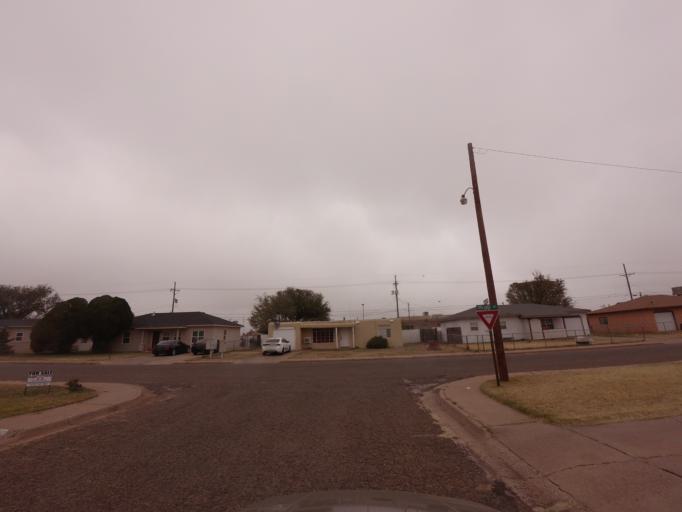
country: US
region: New Mexico
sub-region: Curry County
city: Clovis
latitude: 34.4299
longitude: -103.2086
